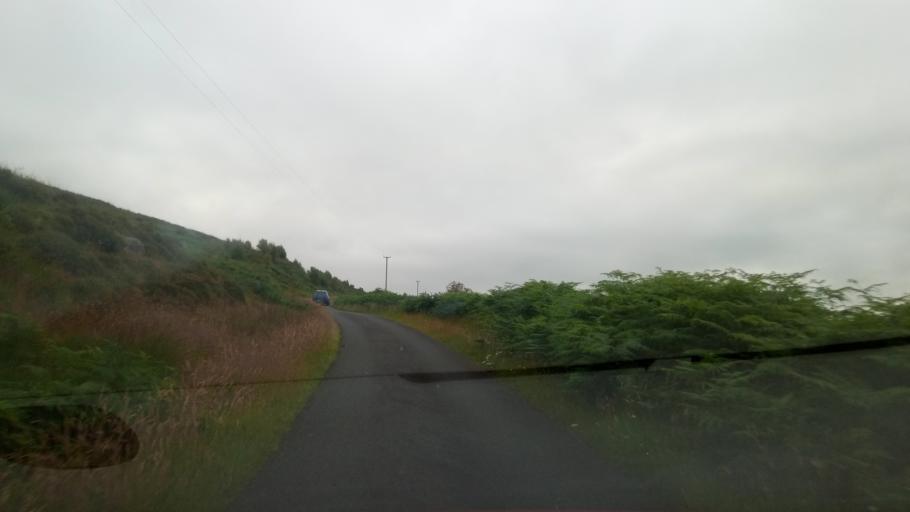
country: GB
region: Scotland
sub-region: Dumfries and Galloway
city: Langholm
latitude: 55.1736
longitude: -2.9368
